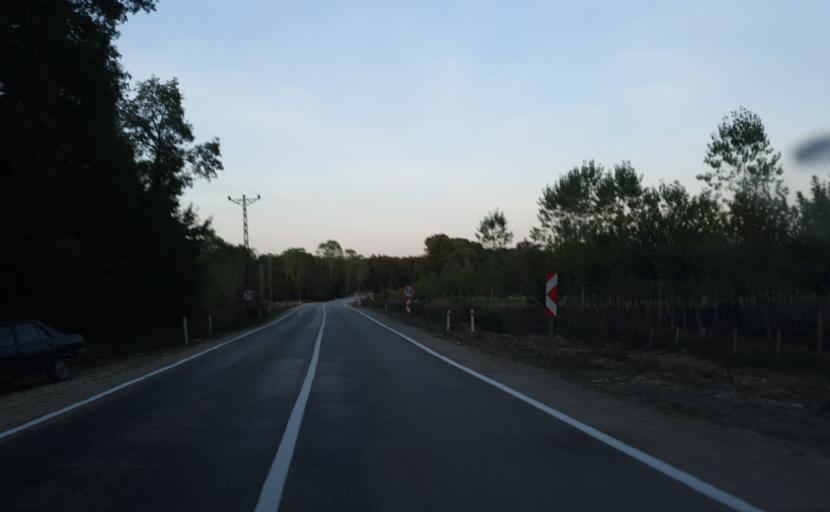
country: TR
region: Kirklareli
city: Igneada
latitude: 41.8754
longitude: 27.9385
